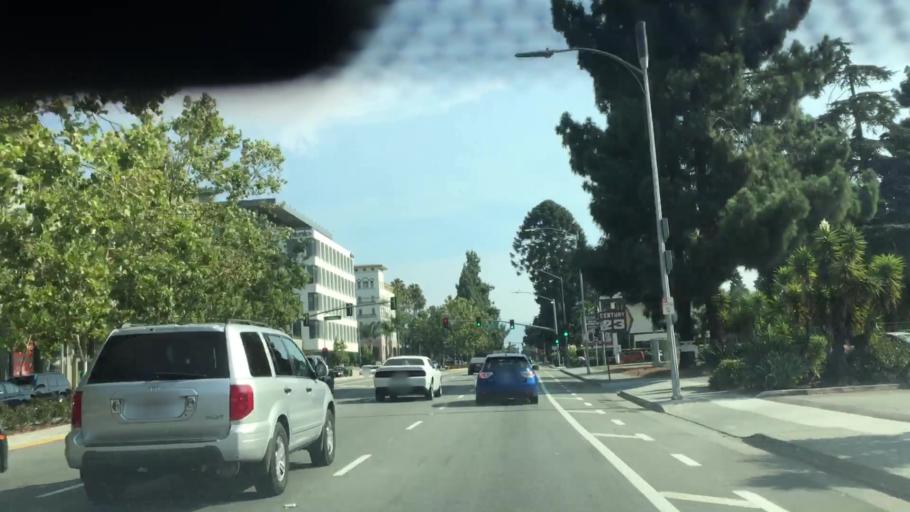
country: US
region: California
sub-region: Santa Clara County
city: Burbank
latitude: 37.3202
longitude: -121.9503
